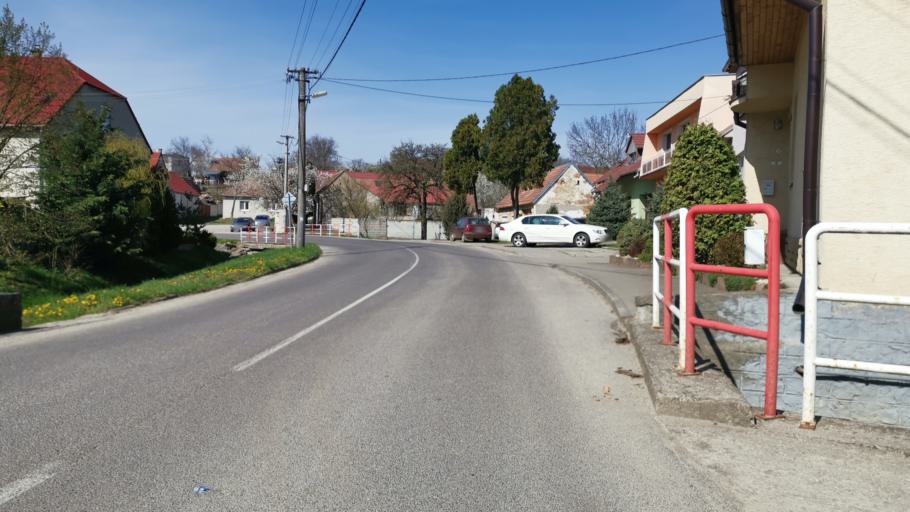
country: SK
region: Trnavsky
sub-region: Okres Skalica
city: Holic
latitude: 48.7490
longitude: 17.2025
